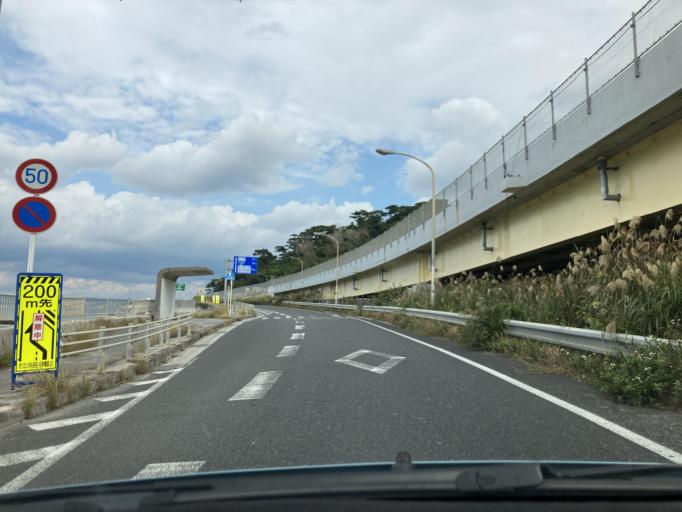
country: JP
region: Okinawa
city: Nago
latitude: 26.5419
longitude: 127.9647
